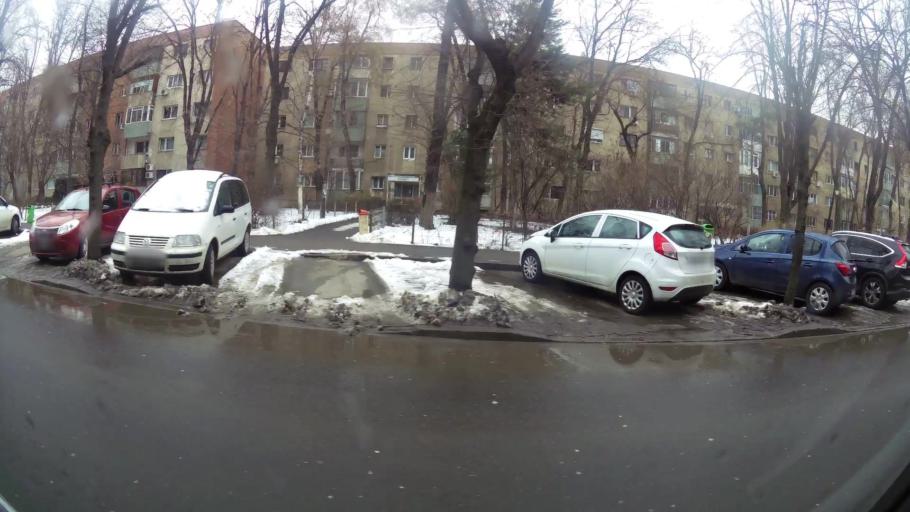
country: RO
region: Ilfov
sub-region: Comuna Chiajna
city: Rosu
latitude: 44.4250
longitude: 26.0249
